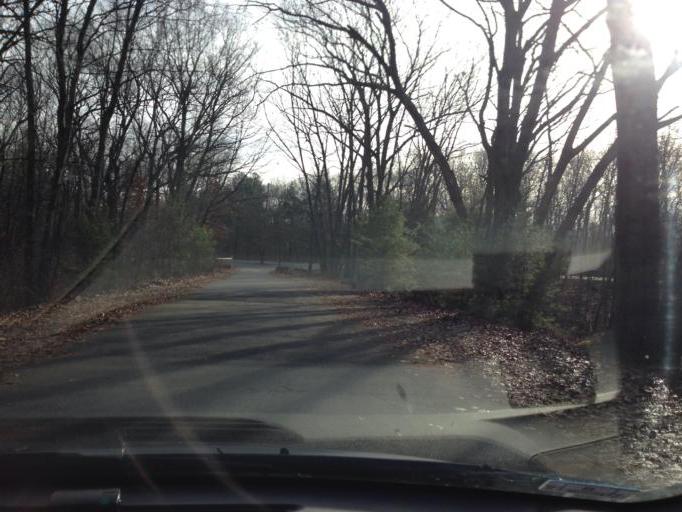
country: US
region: Massachusetts
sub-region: Middlesex County
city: Bedford
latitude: 42.5082
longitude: -71.3108
